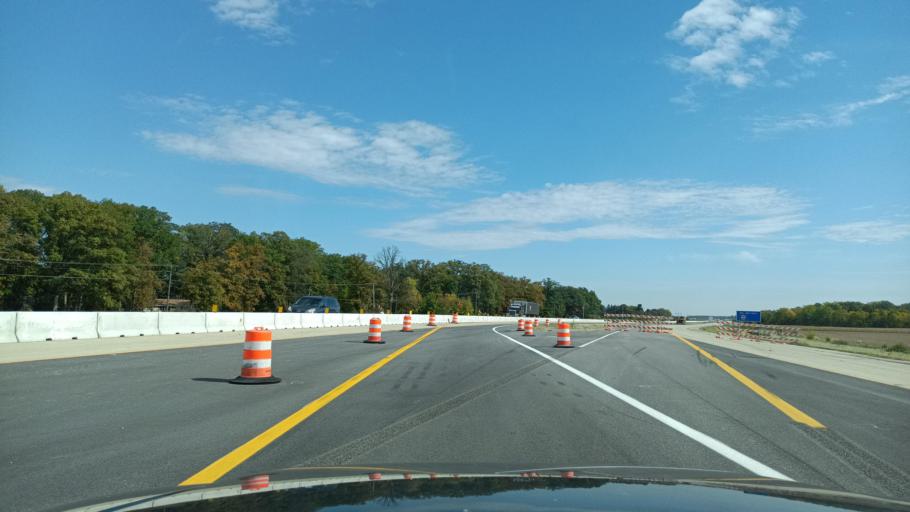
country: US
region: Indiana
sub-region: Allen County
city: New Haven
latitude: 41.1068
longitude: -84.9578
